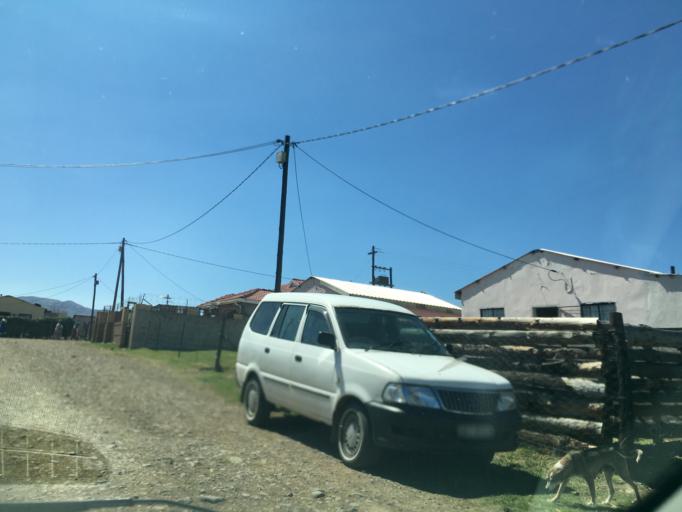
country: ZA
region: Eastern Cape
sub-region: Chris Hani District Municipality
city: Elliot
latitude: -31.3395
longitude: 27.8345
